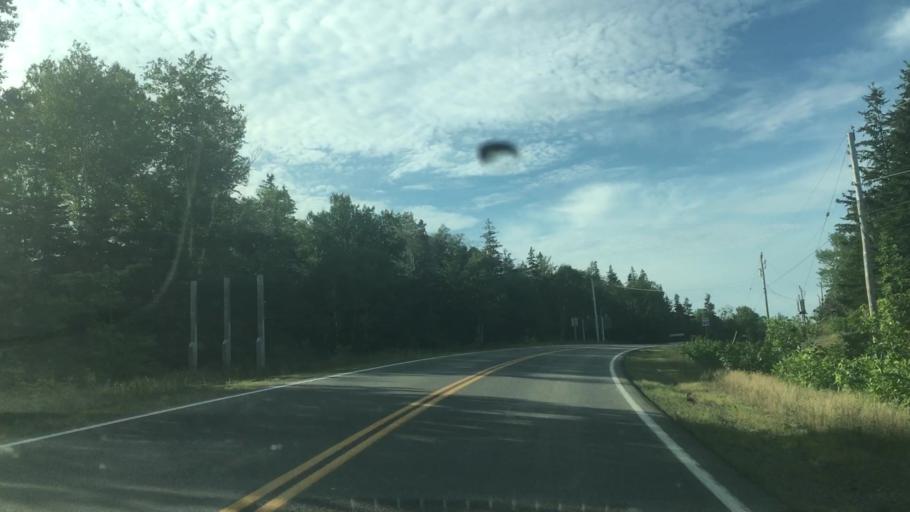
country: CA
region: Nova Scotia
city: Sydney Mines
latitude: 46.8182
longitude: -60.7949
